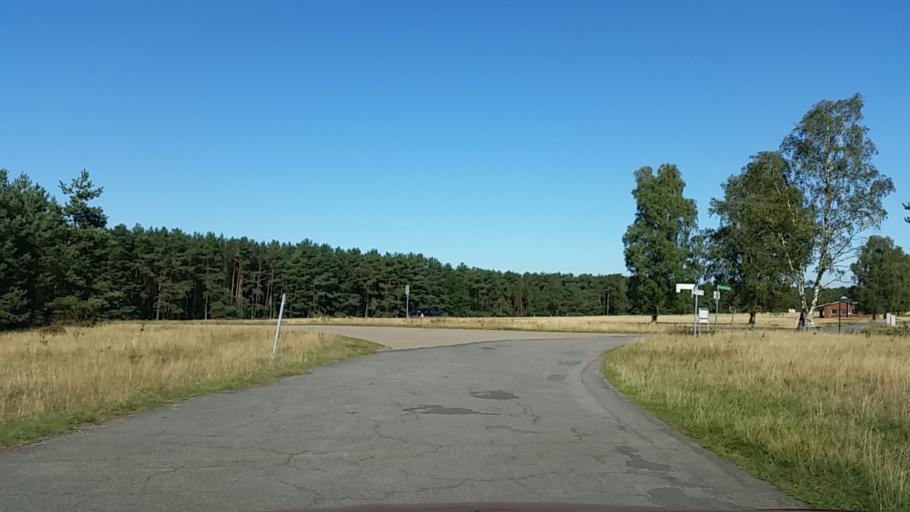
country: DE
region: Lower Saxony
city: Schneverdingen
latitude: 53.1495
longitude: 9.8124
